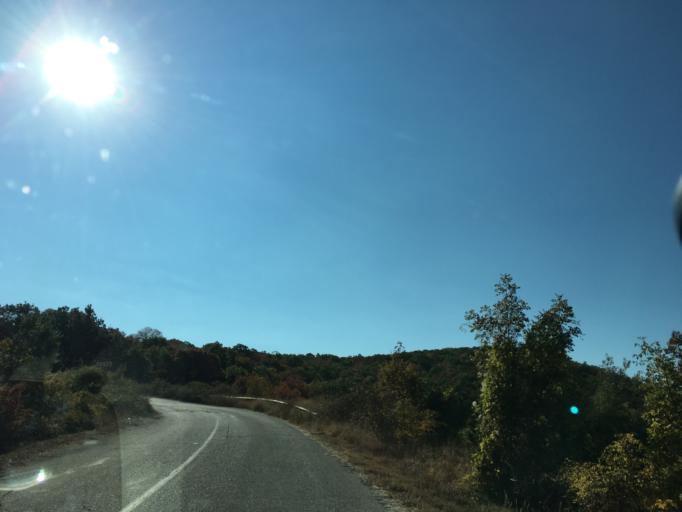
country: BG
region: Khaskovo
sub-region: Obshtina Ivaylovgrad
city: Ivaylovgrad
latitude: 41.4510
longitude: 26.1368
